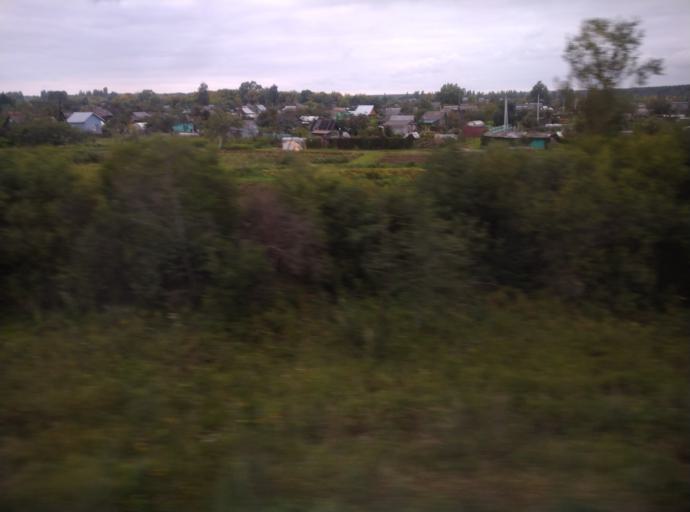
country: RU
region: Kostroma
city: Nerekhta
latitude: 57.4744
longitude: 40.5783
